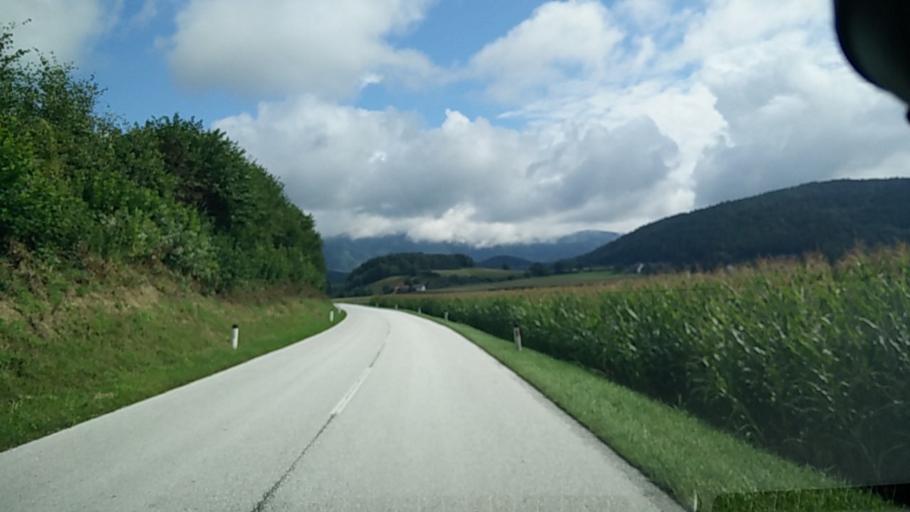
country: AT
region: Carinthia
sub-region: Politischer Bezirk Volkermarkt
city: Voelkermarkt
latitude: 46.6605
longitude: 14.5722
